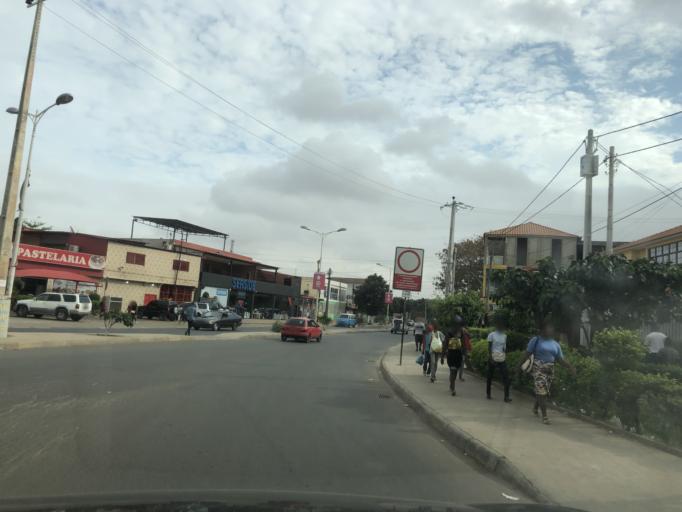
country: AO
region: Luanda
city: Luanda
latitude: -8.9116
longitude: 13.3715
